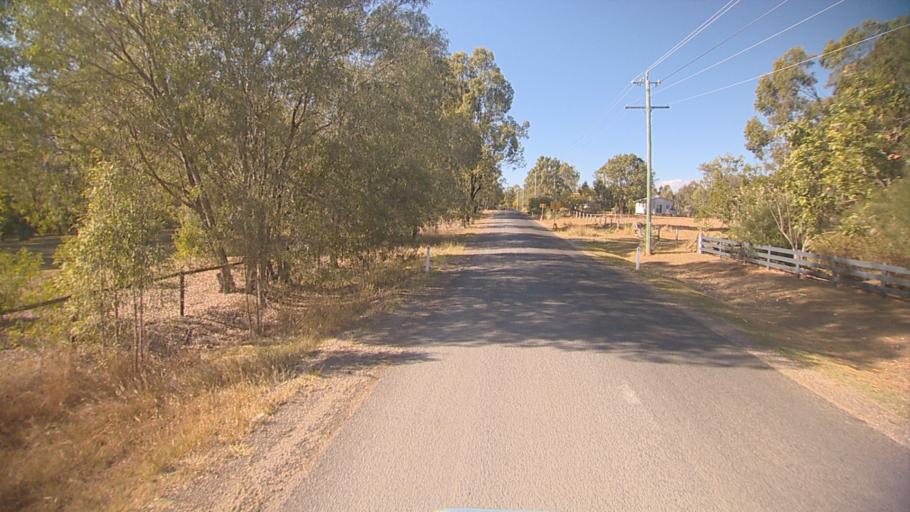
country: AU
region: Queensland
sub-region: Logan
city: Cedar Vale
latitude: -27.8363
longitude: 152.9947
